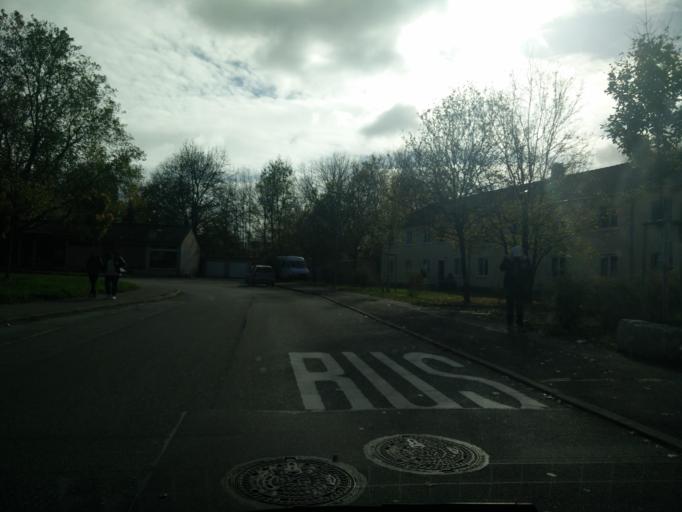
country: DE
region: Baden-Wuerttemberg
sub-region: Regierungsbezirk Stuttgart
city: Ditzingen
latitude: 48.8147
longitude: 9.0820
